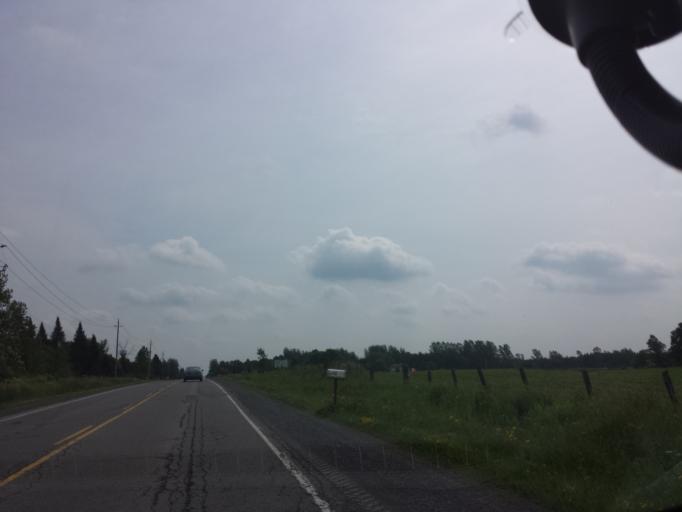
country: CA
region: Ontario
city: Bourget
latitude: 45.4051
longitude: -75.2649
